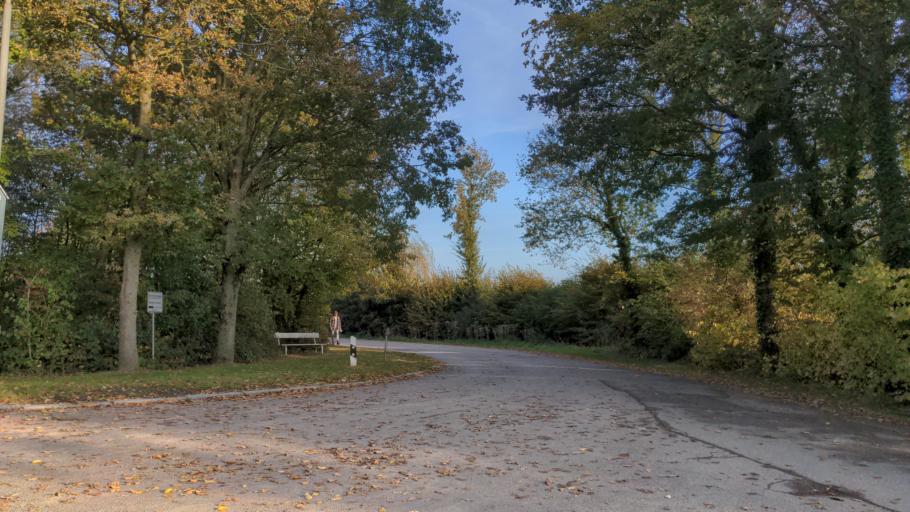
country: DE
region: Schleswig-Holstein
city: Manhagen
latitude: 54.1988
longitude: 10.9263
